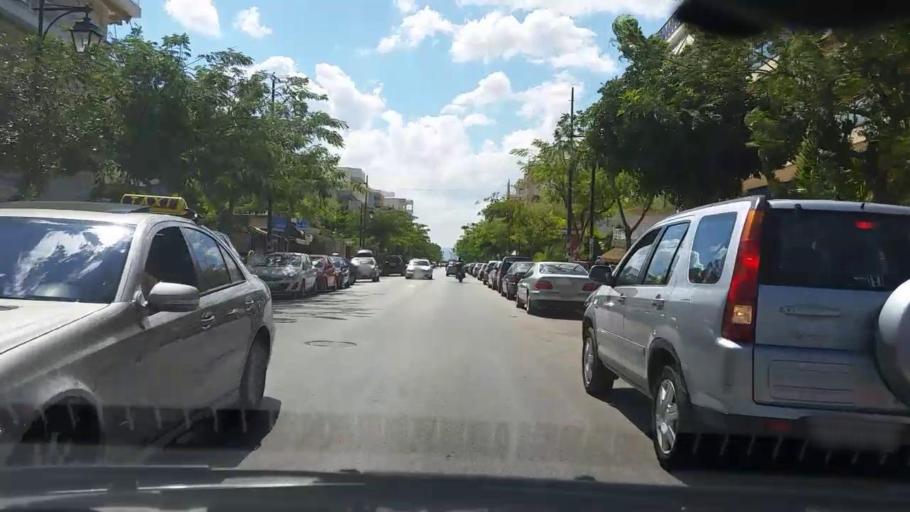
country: GR
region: Peloponnese
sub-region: Nomos Korinthias
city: Loutraki
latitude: 37.9722
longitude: 22.9778
